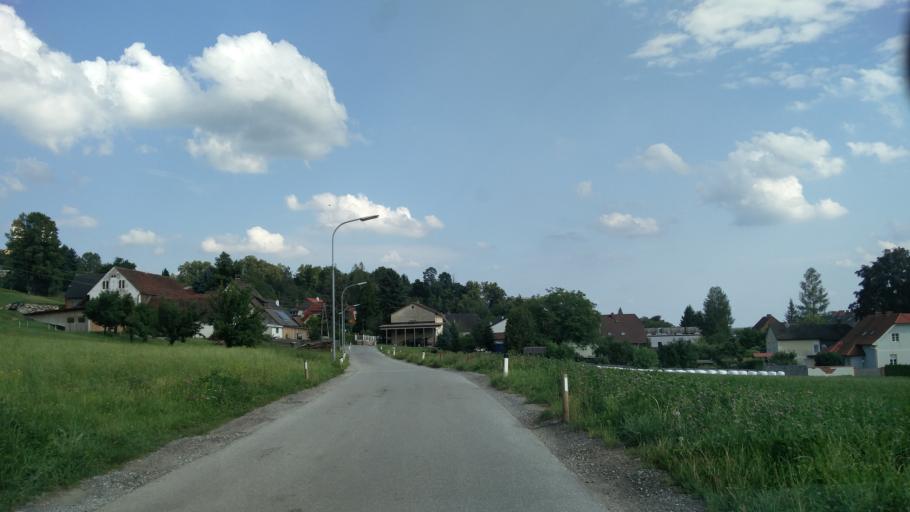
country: AT
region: Styria
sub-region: Politischer Bezirk Weiz
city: Weiz
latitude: 47.2251
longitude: 15.6271
